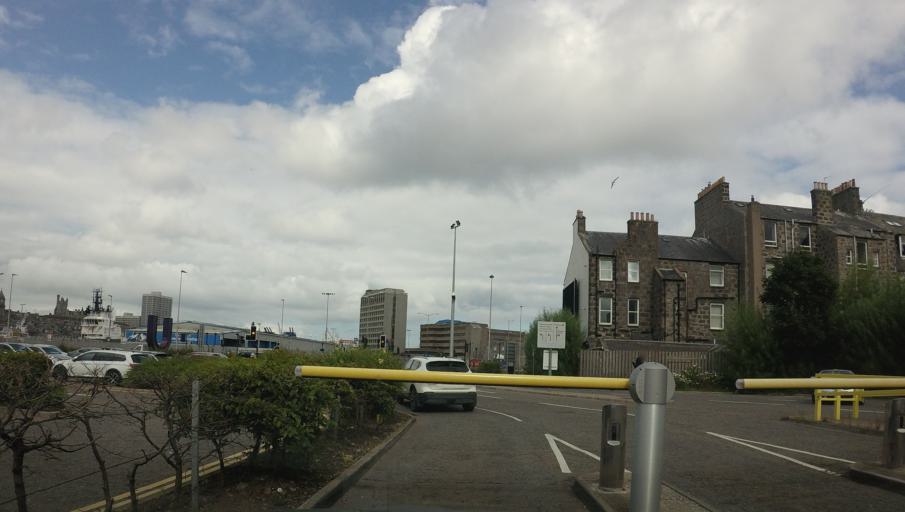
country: GB
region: Scotland
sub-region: Aberdeen City
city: Aberdeen
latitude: 57.1430
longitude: -2.0941
